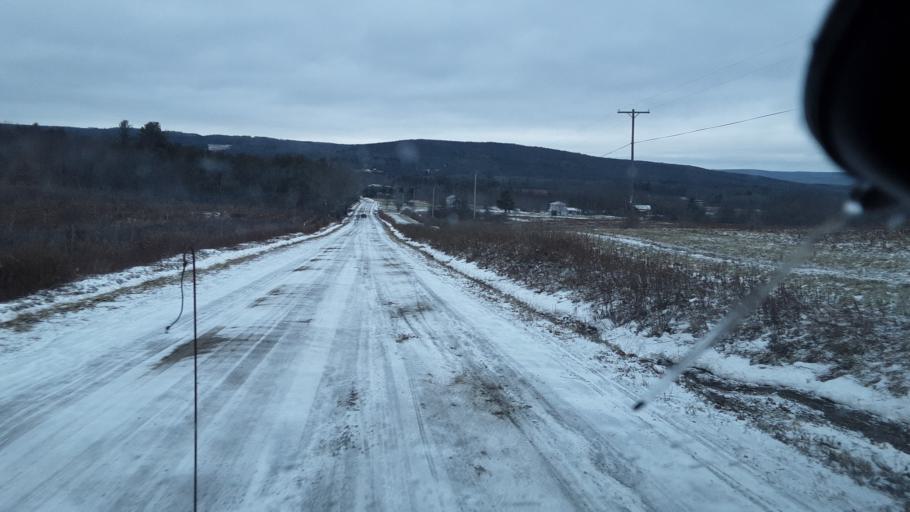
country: US
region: New York
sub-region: Allegany County
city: Friendship
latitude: 42.2892
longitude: -78.1624
